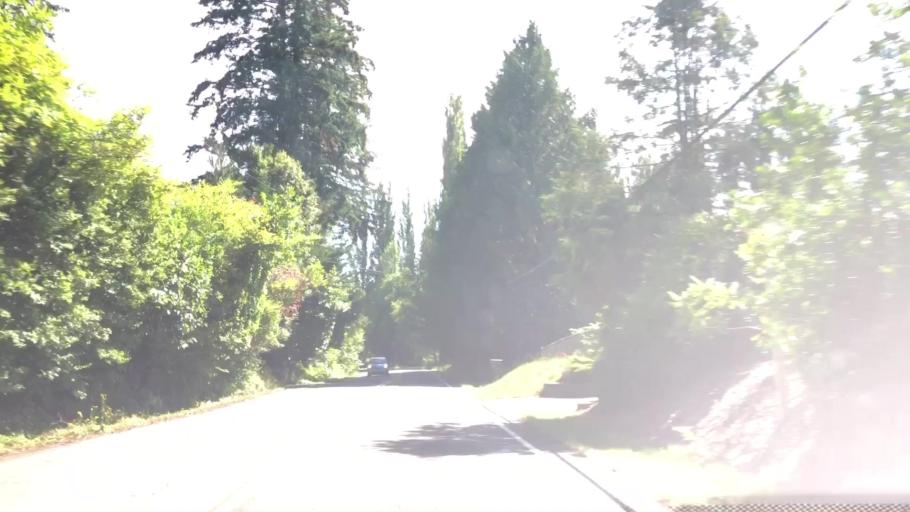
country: US
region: Washington
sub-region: King County
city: Cottage Lake
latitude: 47.7250
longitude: -122.0773
